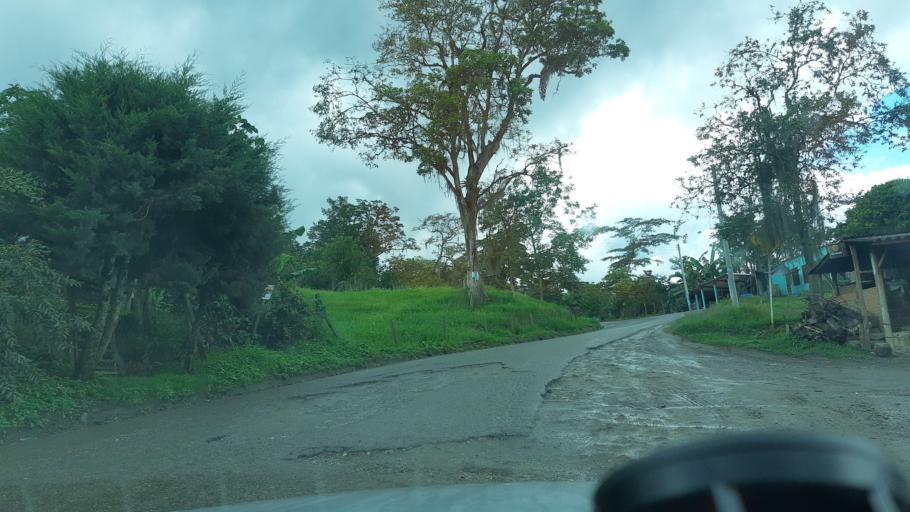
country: CO
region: Boyaca
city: Chinavita
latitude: 5.1299
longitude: -73.3636
